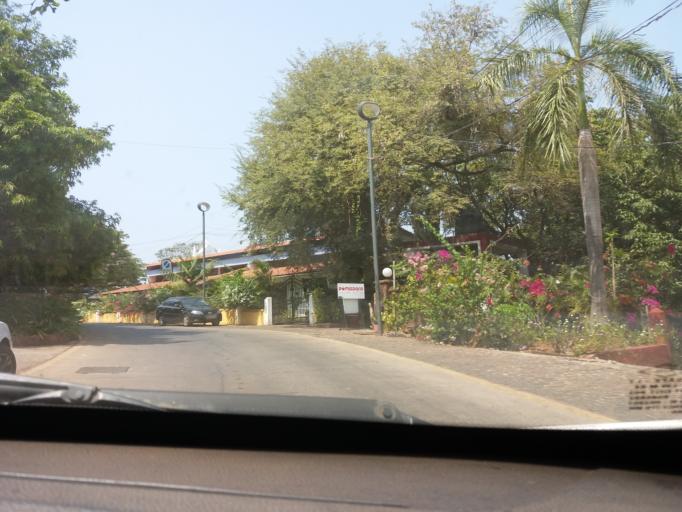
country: IN
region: Goa
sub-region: North Goa
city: Taleigao
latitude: 15.4547
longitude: 73.8032
